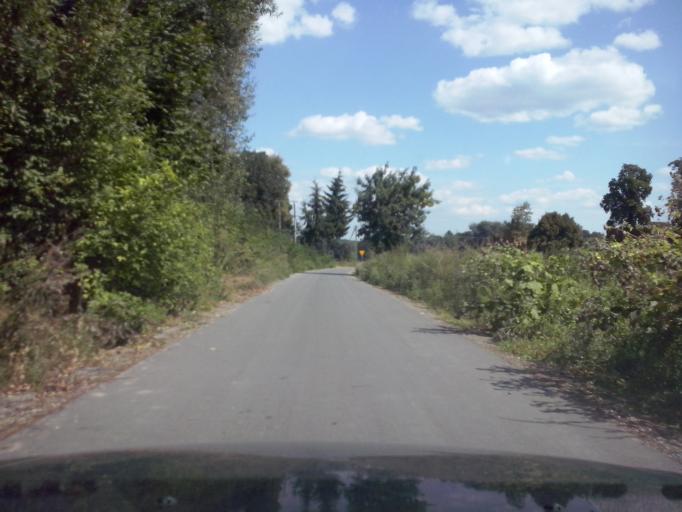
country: PL
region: Swietokrzyskie
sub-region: Powiat staszowski
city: Staszow
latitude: 50.5948
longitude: 21.0924
